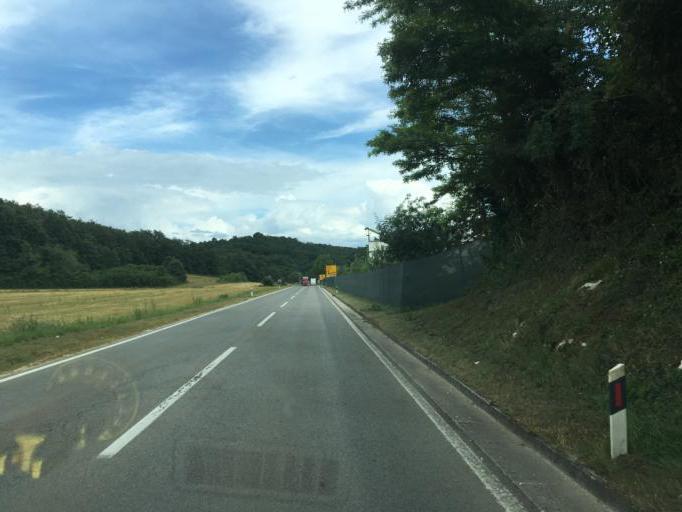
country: HR
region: Istarska
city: Pazin
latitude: 45.2425
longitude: 13.9066
